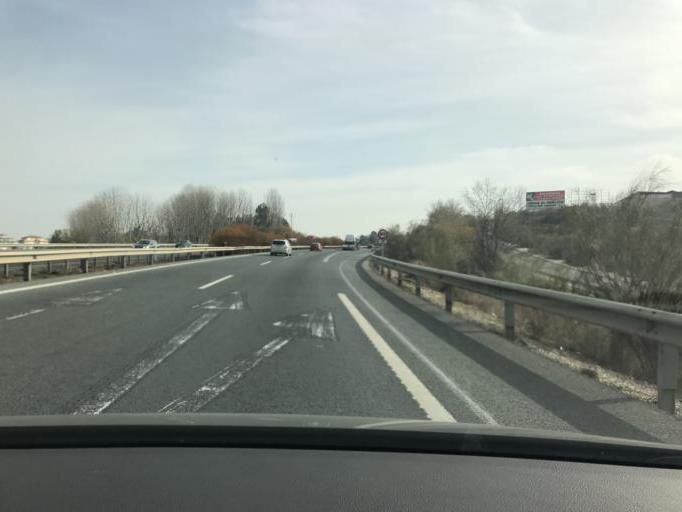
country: ES
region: Andalusia
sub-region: Provincia de Granada
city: Lachar
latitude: 37.1941
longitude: -3.8424
